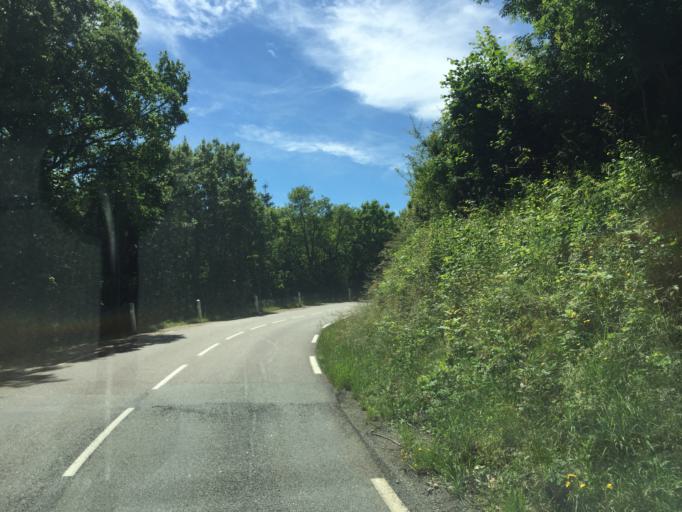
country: FR
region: Rhone-Alpes
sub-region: Departement de la Savoie
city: Saint-Baldoph
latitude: 45.5076
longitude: 5.9236
